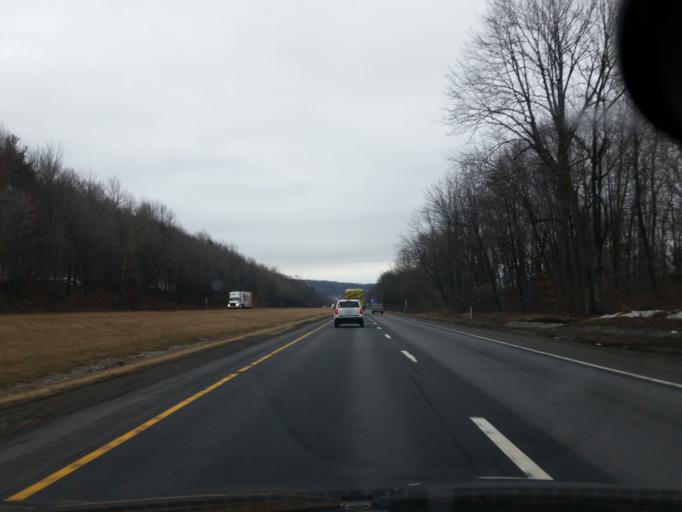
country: US
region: Pennsylvania
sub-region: Susquehanna County
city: Susquehanna
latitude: 41.8389
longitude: -75.6818
